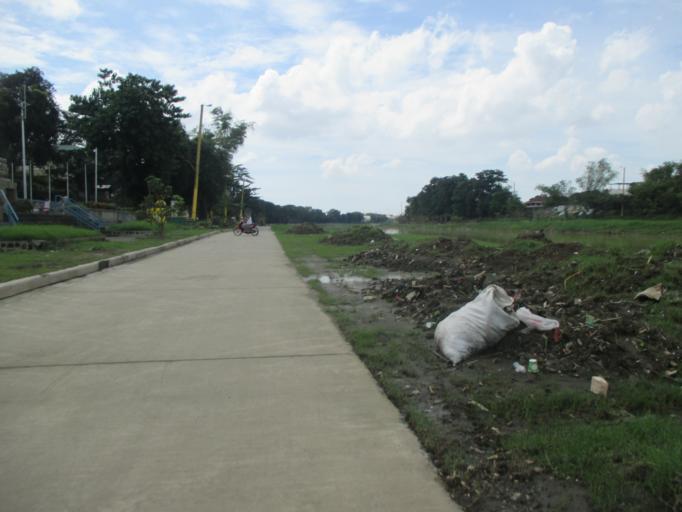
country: PH
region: Metro Manila
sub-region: Marikina
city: Calumpang
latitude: 14.6323
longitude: 121.0940
